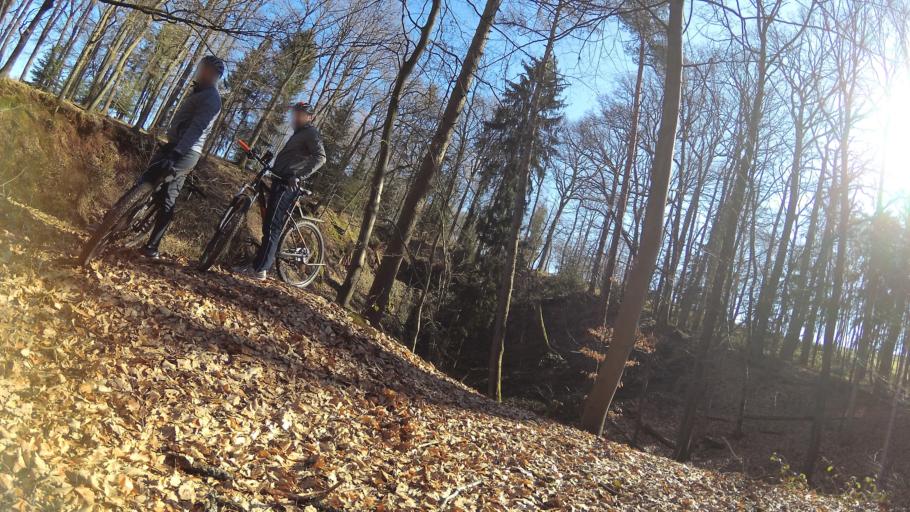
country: DE
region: Saarland
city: Hangard
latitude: 49.4112
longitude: 7.1971
